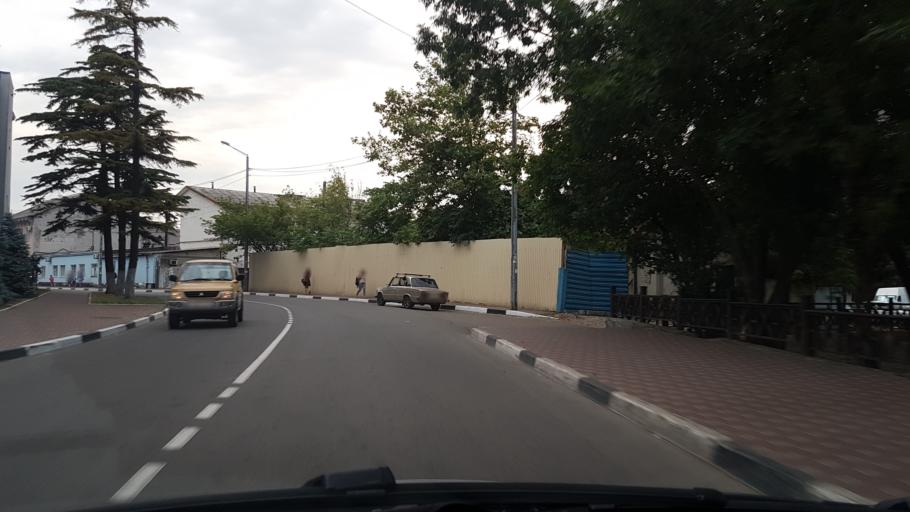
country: RU
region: Krasnodarskiy
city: Tuapse
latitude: 44.0935
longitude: 39.0794
